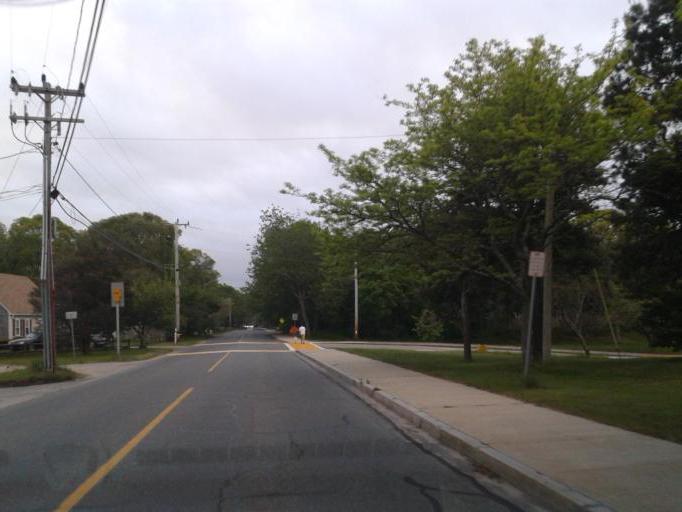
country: US
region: Massachusetts
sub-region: Barnstable County
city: Teaticket
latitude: 41.5679
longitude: -70.5894
